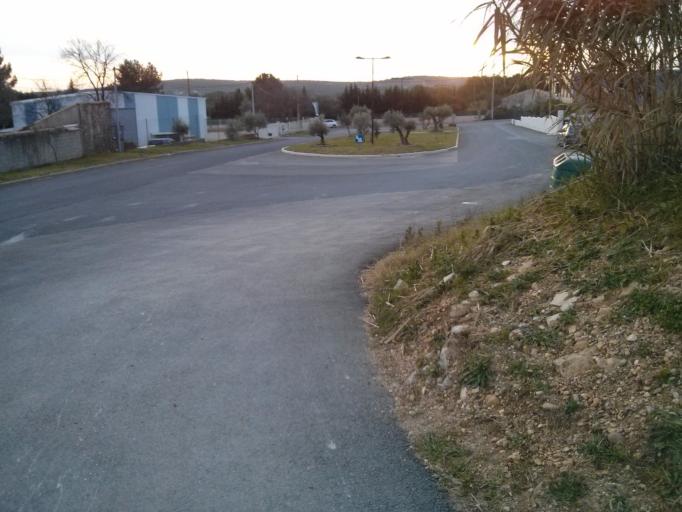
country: FR
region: Languedoc-Roussillon
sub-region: Departement du Gard
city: Aubais
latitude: 43.7461
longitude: 4.1435
